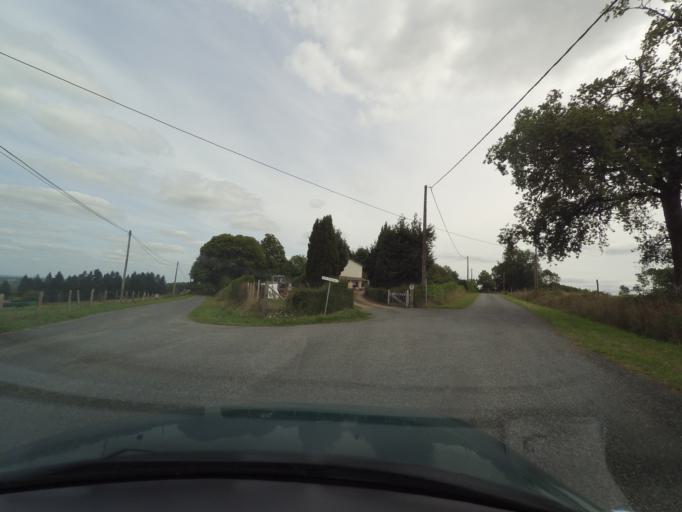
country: FR
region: Limousin
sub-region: Departement de la Haute-Vienne
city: Ladignac-le-Long
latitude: 45.6420
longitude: 1.1174
